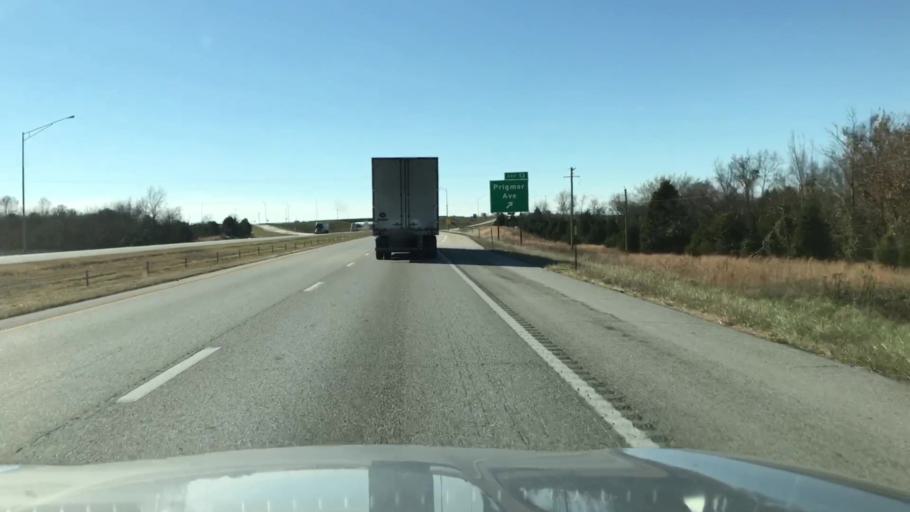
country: US
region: Missouri
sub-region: Jasper County
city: Duenweg
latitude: 37.0713
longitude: -94.3987
